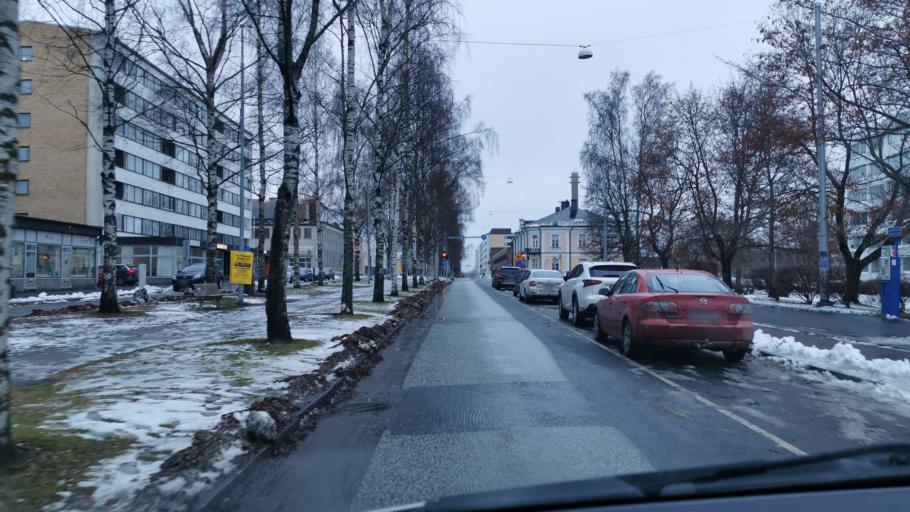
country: FI
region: Ostrobothnia
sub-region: Vaasa
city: Vaasa
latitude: 63.0959
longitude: 21.6092
